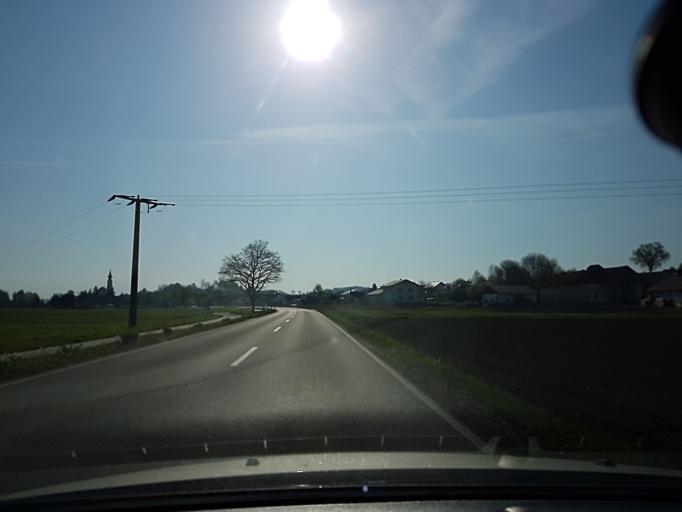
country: DE
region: Bavaria
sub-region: Lower Bavaria
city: Altfraunhofen
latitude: 48.4485
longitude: 12.1571
